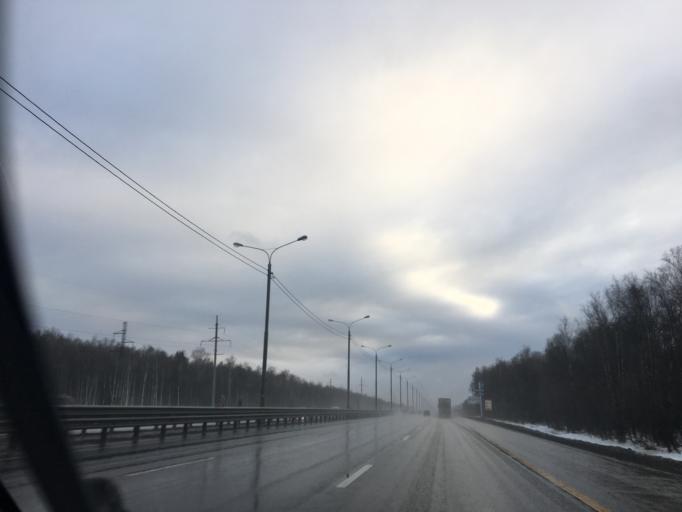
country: RU
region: Moskovskaya
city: L'vovskiy
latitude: 55.2879
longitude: 37.5426
